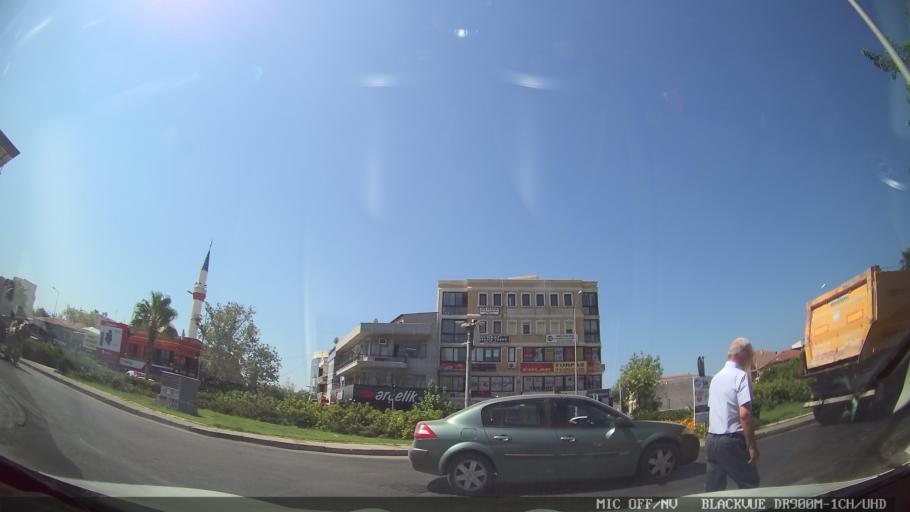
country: TR
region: Izmir
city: Karsiyaka
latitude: 38.4940
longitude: 27.0625
